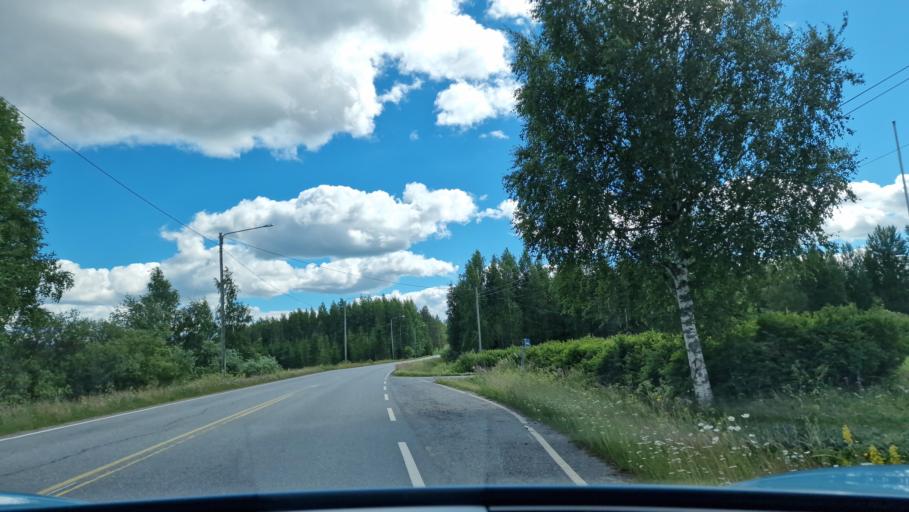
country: FI
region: Southern Ostrobothnia
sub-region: Jaerviseutu
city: Soini
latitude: 62.8422
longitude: 24.3281
